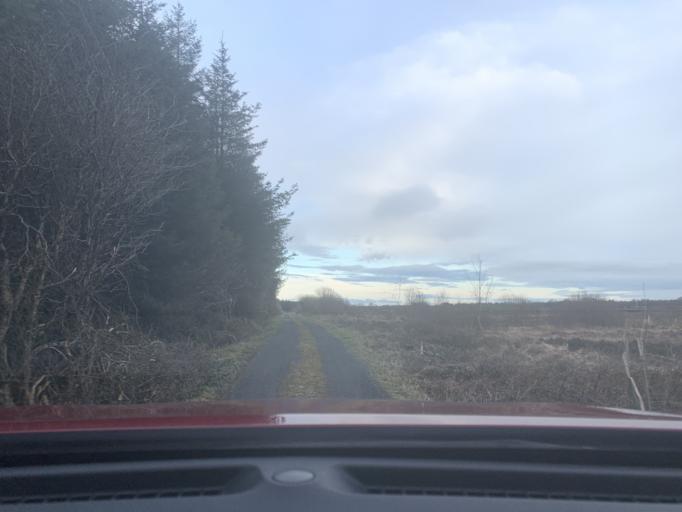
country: IE
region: Connaught
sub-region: Roscommon
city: Ballaghaderreen
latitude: 53.8889
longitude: -8.5810
